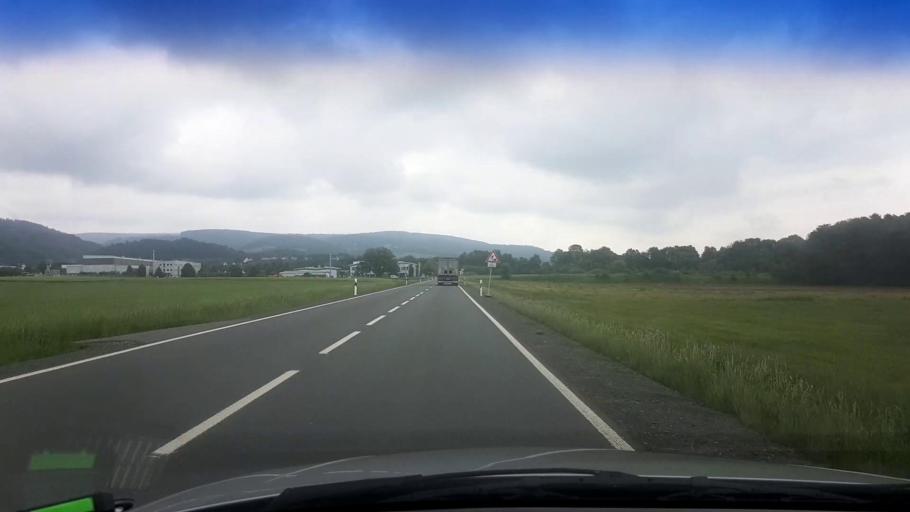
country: DE
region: Bavaria
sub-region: Upper Franconia
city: Gesees
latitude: 50.0157
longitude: 11.6672
